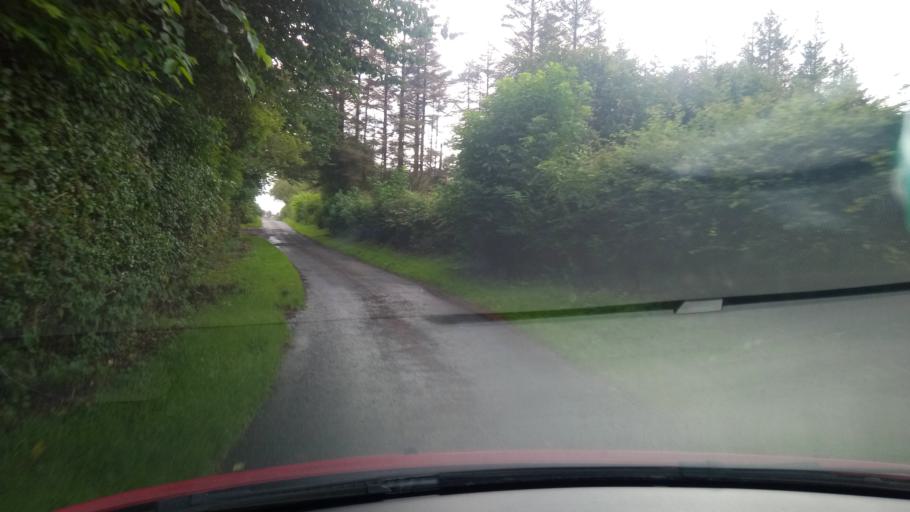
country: GB
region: Scotland
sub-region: The Scottish Borders
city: Hawick
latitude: 55.4263
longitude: -2.7550
